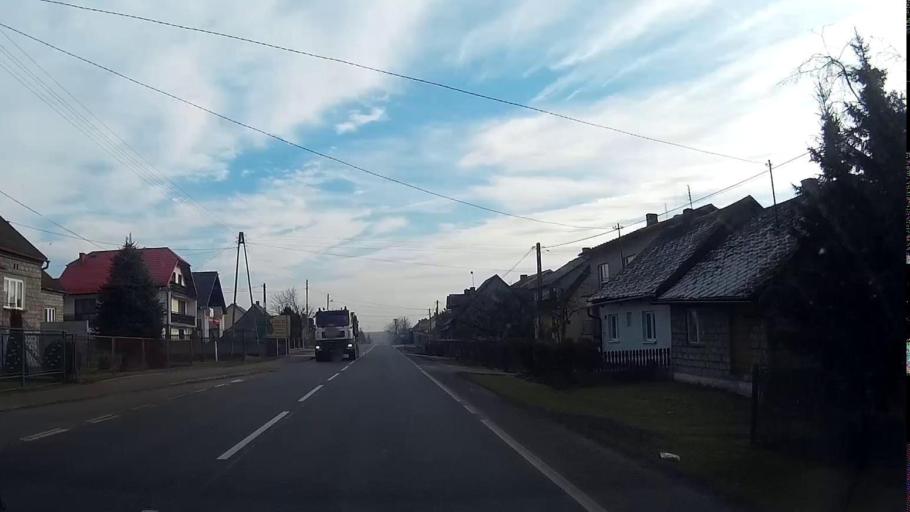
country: PL
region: Lesser Poland Voivodeship
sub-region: Powiat krakowski
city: Kaszow
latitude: 50.0397
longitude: 19.7329
